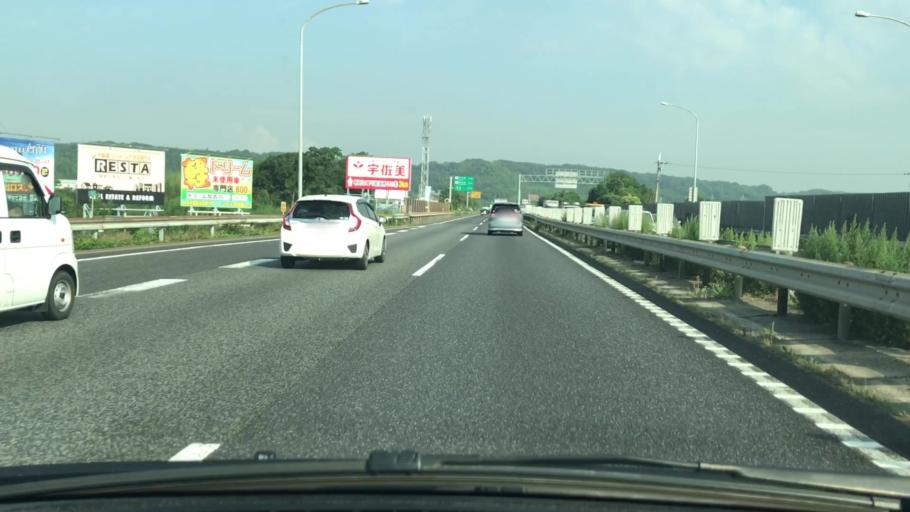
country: JP
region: Hyogo
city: Akashi
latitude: 34.6857
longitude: 134.9785
